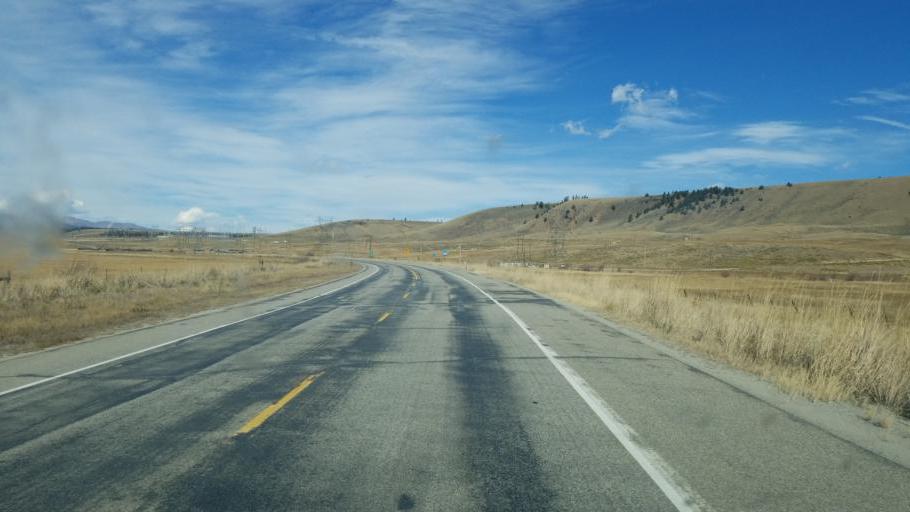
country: US
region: Colorado
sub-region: Lake County
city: Leadville
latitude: 39.1727
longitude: -106.3219
